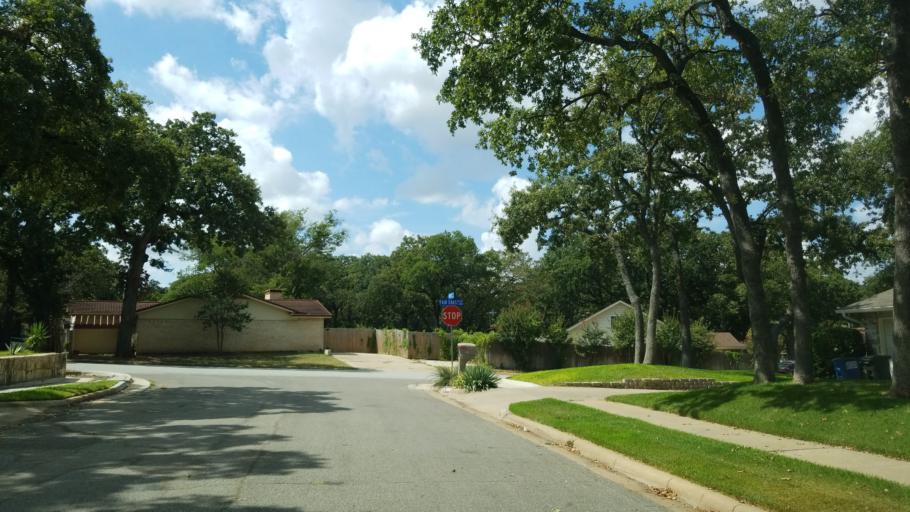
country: US
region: Texas
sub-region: Tarrant County
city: Euless
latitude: 32.8558
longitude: -97.0874
